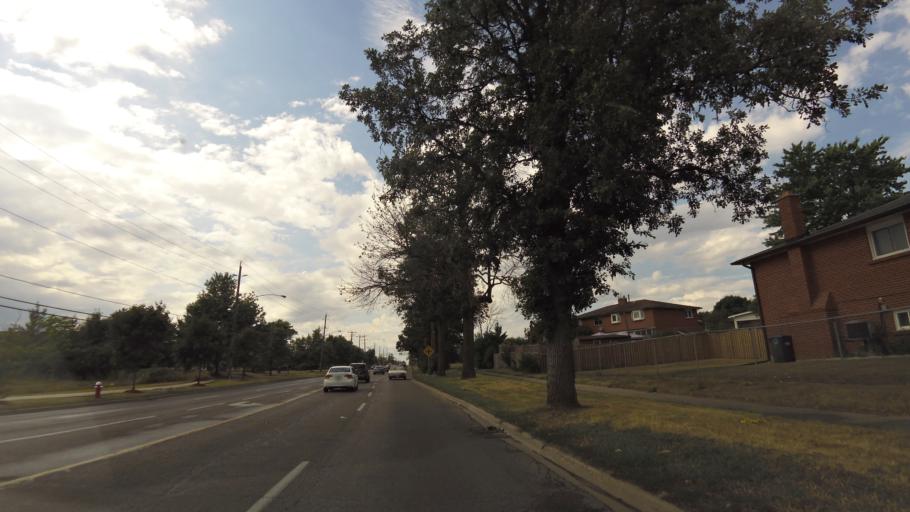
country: CA
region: Ontario
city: Brampton
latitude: 43.6687
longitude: -79.7604
